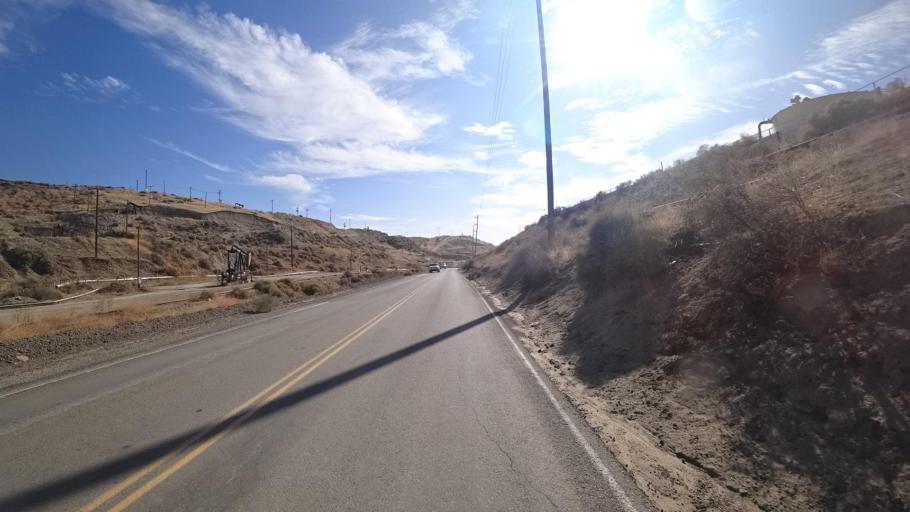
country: US
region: California
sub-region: Kern County
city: Oildale
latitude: 35.5825
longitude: -118.9592
